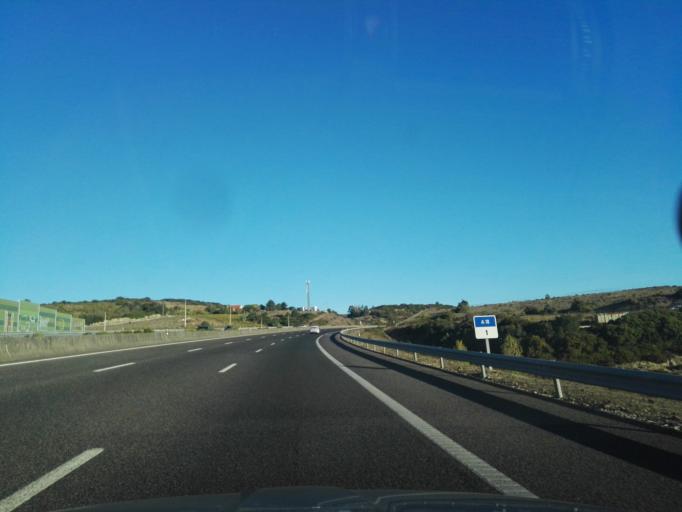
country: PT
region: Lisbon
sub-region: Loures
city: Bucelas
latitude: 38.9204
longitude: -9.0749
